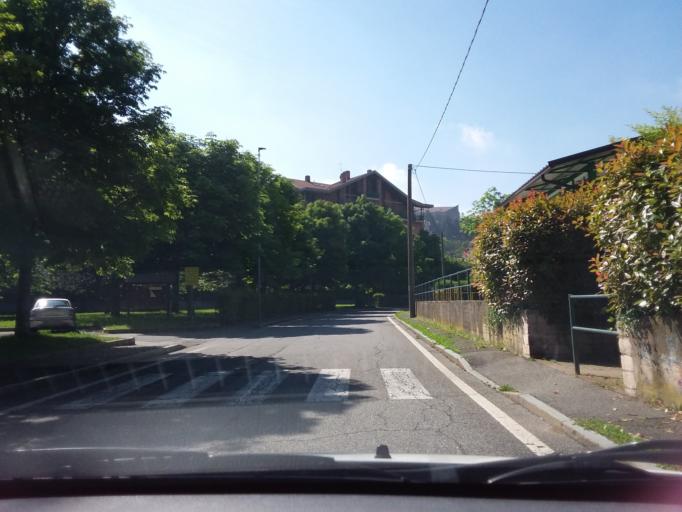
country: IT
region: Piedmont
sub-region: Provincia di Torino
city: Rivoli
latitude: 45.0743
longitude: 7.5074
